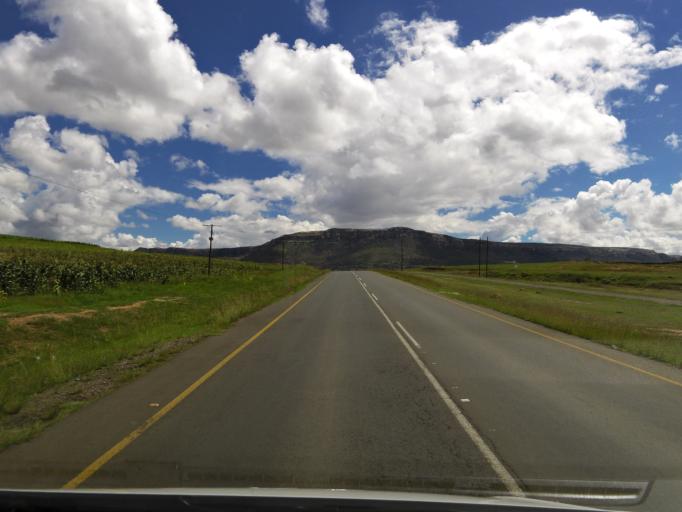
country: LS
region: Maseru
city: Maseru
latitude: -29.4606
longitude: 27.5410
